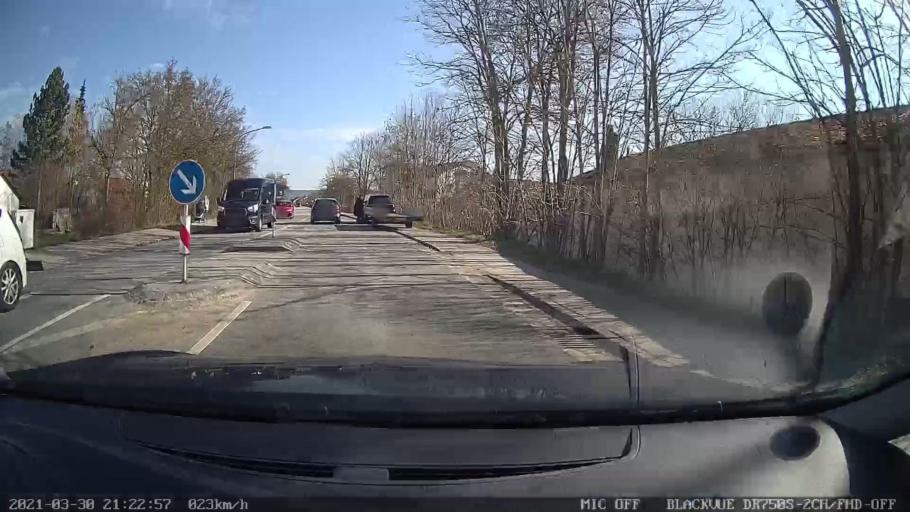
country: DE
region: Bavaria
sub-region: Upper Palatinate
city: Zeitlarn
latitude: 49.0778
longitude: 12.1106
